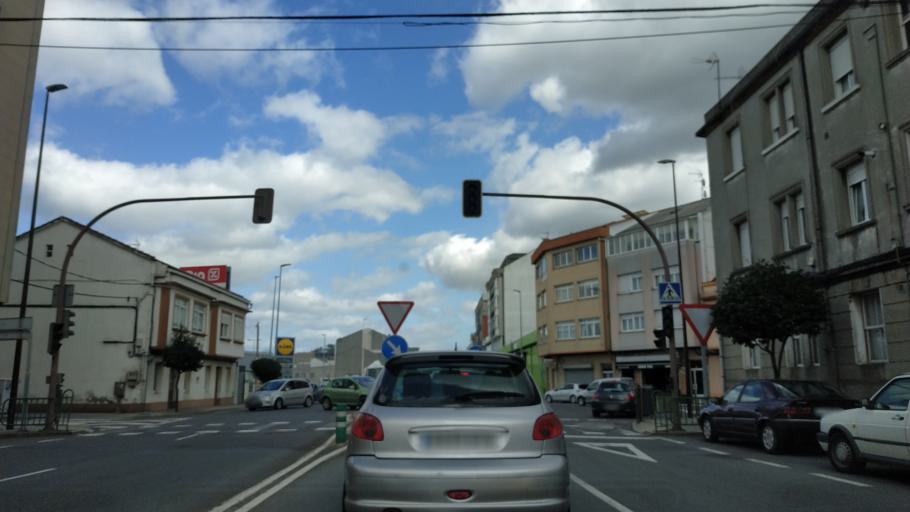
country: ES
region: Galicia
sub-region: Provincia da Coruna
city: Carballo
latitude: 43.2209
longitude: -8.6856
